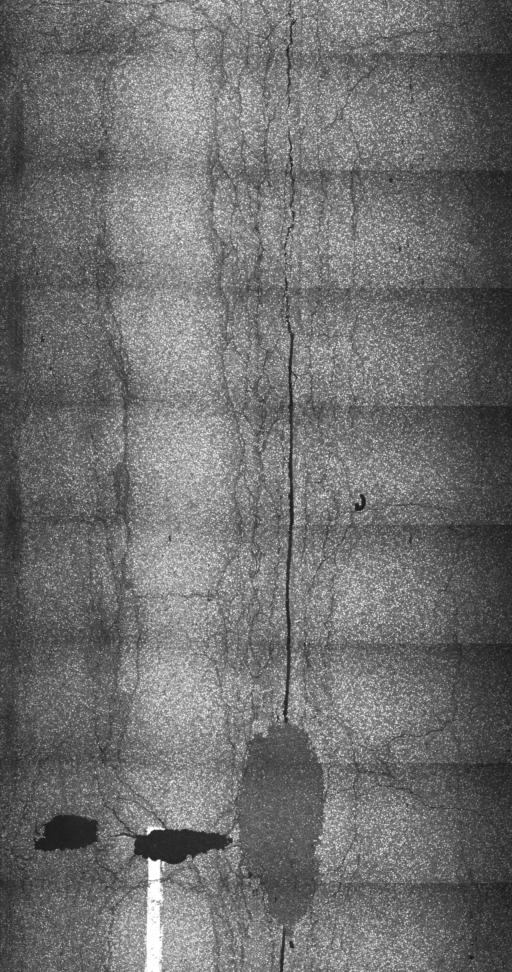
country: US
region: Vermont
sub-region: Washington County
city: South Barre
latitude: 44.1738
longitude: -72.5090
